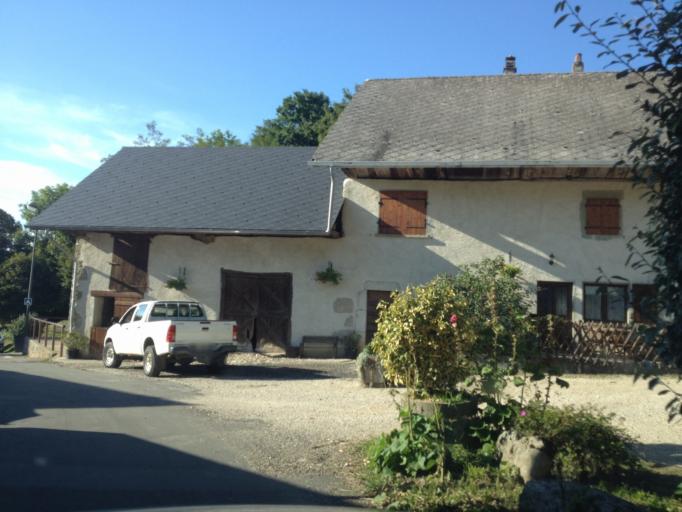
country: FR
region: Rhone-Alpes
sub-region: Departement de la Savoie
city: Mery
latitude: 45.6625
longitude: 5.9433
